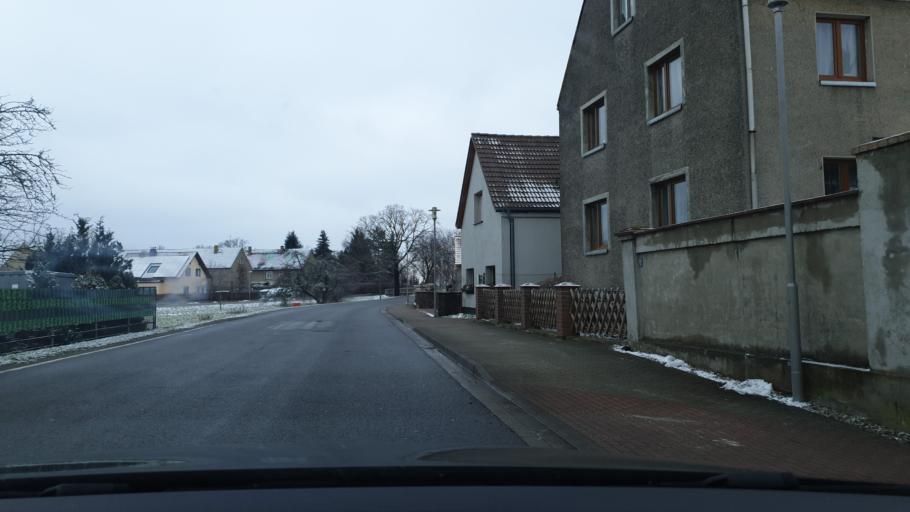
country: DE
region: Saxony
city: Borsdorf
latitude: 51.3110
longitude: 12.5183
